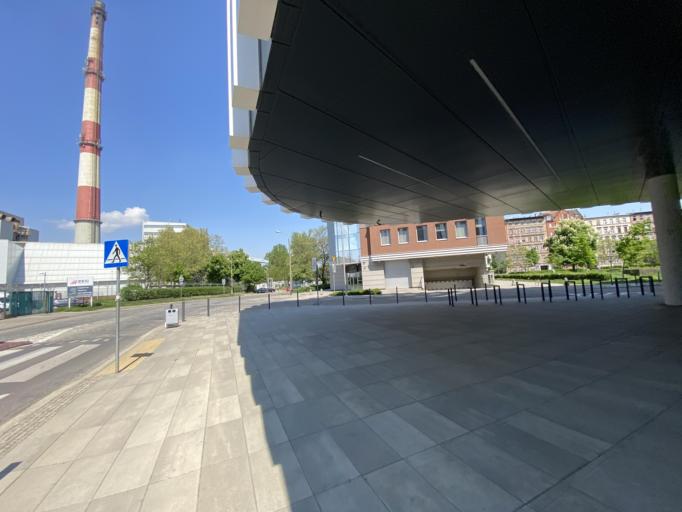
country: PL
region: Lower Silesian Voivodeship
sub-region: Powiat wroclawski
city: Wroclaw
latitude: 51.1221
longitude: 17.0265
